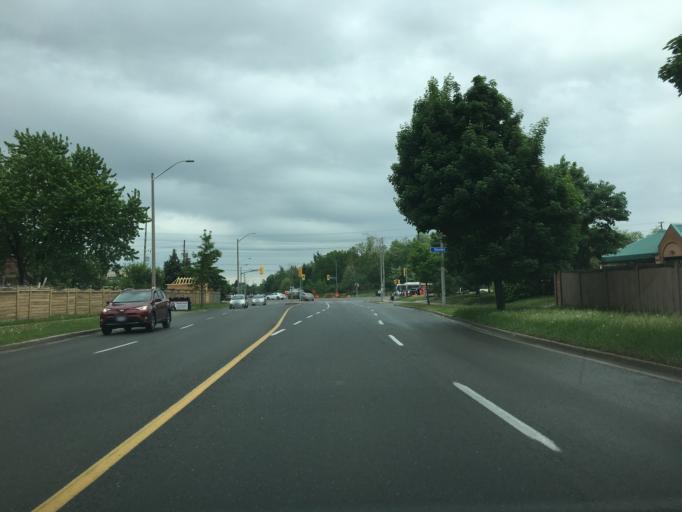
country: CA
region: Ontario
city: Markham
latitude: 43.8339
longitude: -79.2683
